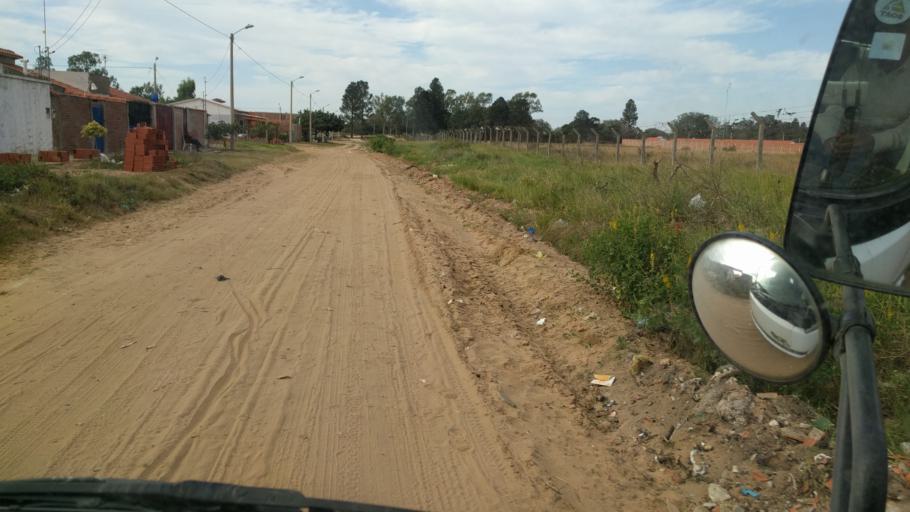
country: BO
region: Santa Cruz
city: Santa Cruz de la Sierra
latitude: -17.6853
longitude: -63.1427
